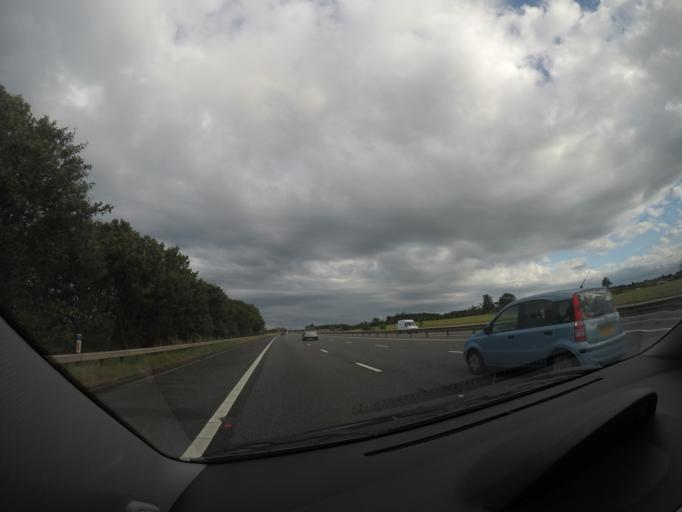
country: GB
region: England
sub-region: Cumbria
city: Scotby
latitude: 54.7871
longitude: -2.8615
